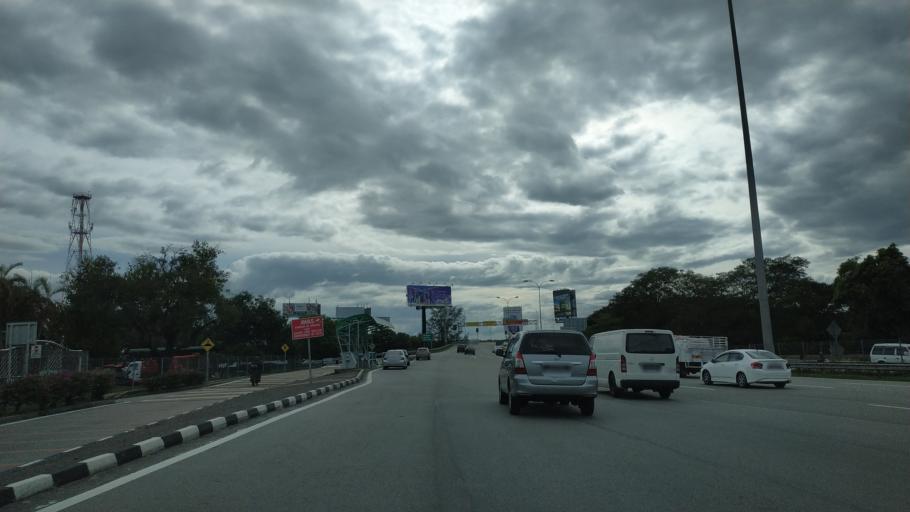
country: MY
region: Penang
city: Perai
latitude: 5.3562
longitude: 100.3926
